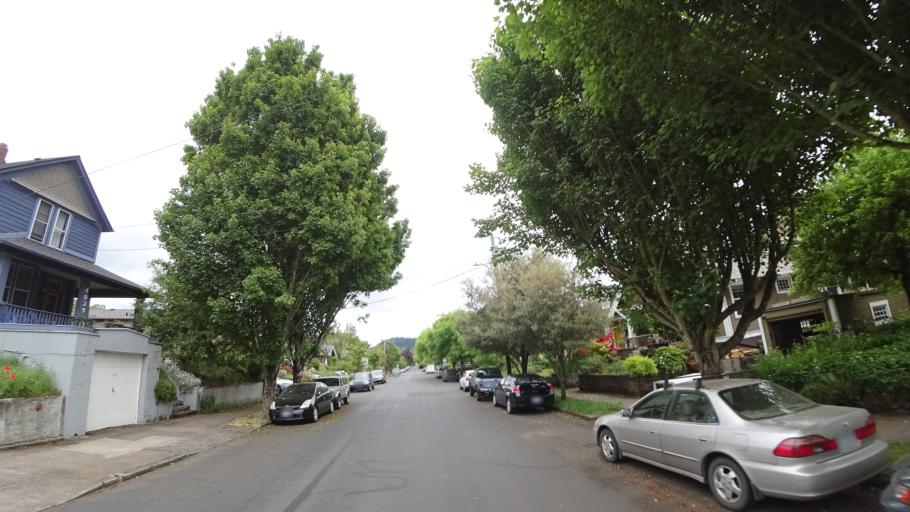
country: US
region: Oregon
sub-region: Multnomah County
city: Portland
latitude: 45.5150
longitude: -122.6211
